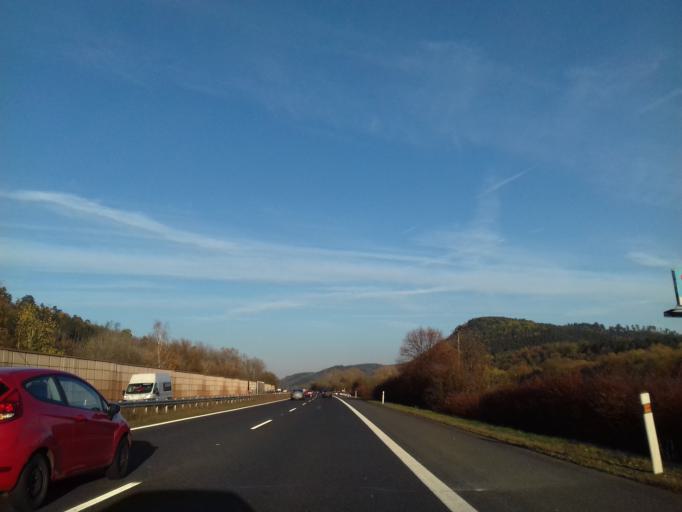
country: CZ
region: Central Bohemia
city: Zdice
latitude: 49.9135
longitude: 13.9908
